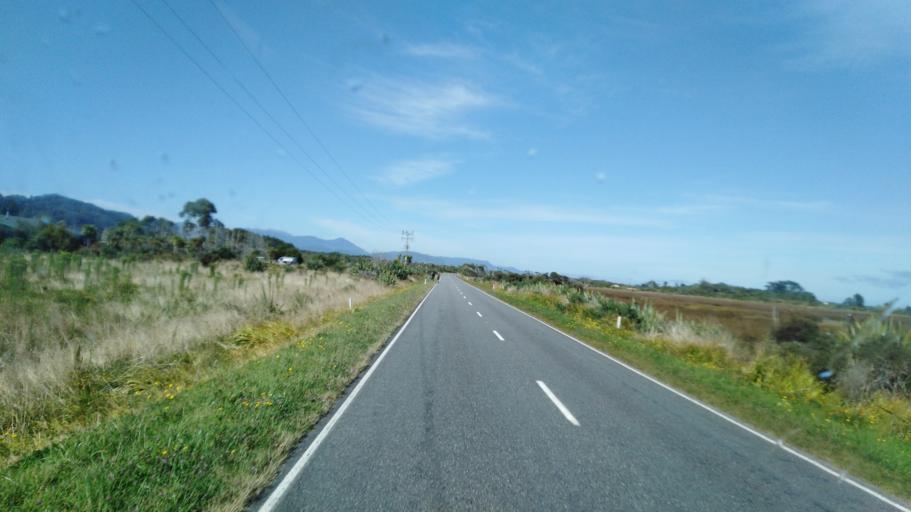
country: NZ
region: West Coast
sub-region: Buller District
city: Westport
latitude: -41.2857
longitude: 172.1038
